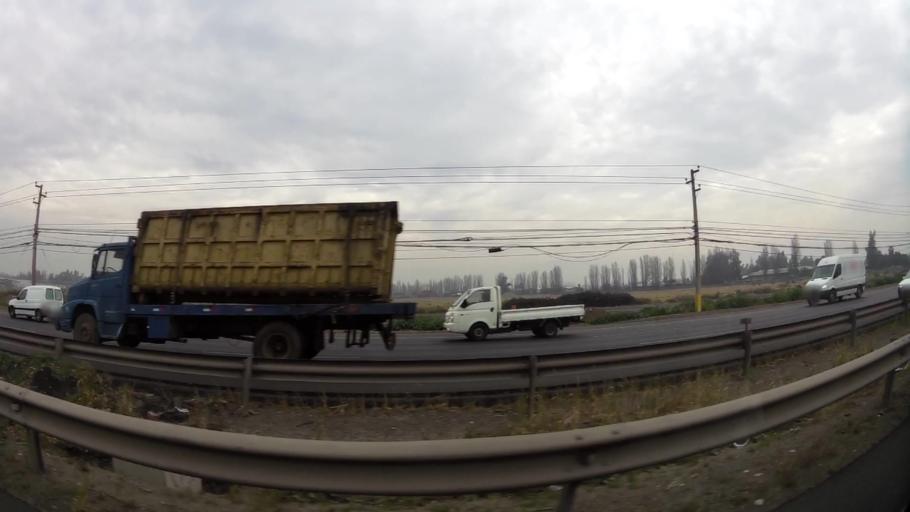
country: CL
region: Santiago Metropolitan
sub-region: Provincia de Chacabuco
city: Chicureo Abajo
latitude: -33.2856
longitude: -70.7364
